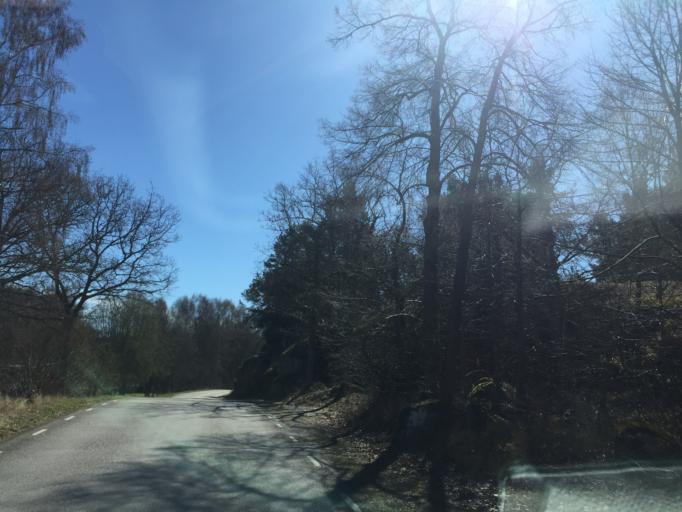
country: SE
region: Kalmar
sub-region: Oskarshamns Kommun
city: Oskarshamn
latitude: 57.2412
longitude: 16.4746
